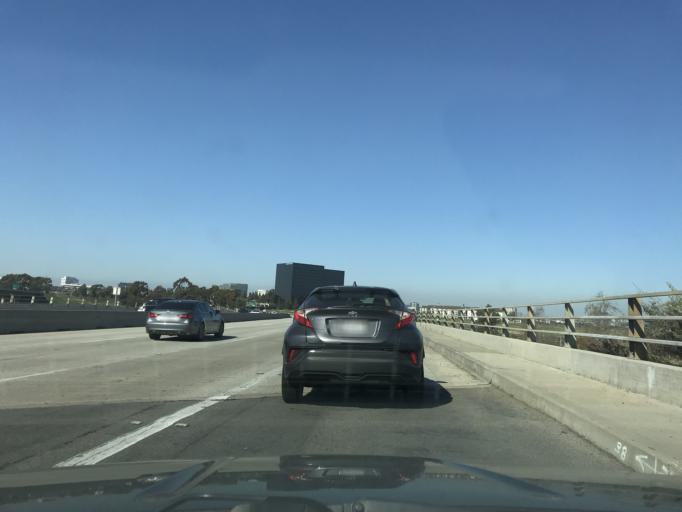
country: US
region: California
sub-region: Orange County
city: Irvine
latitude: 33.6486
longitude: -117.8596
